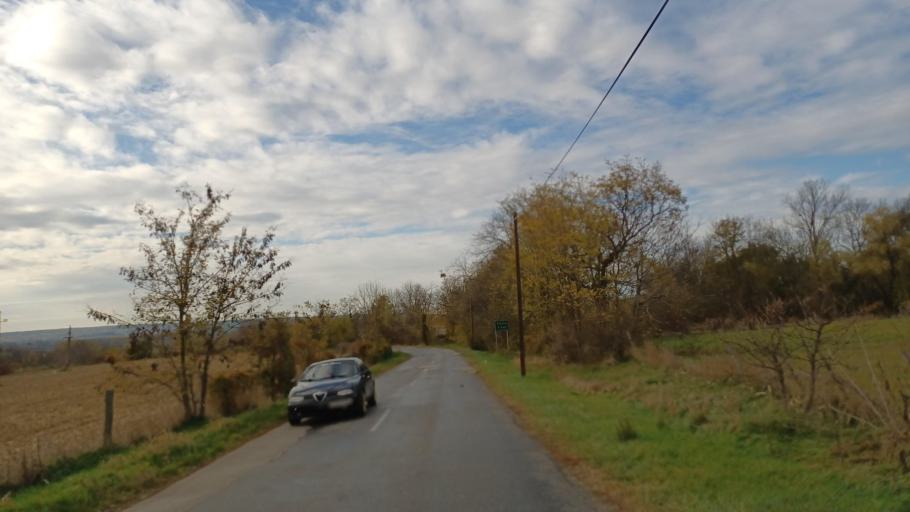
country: HU
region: Fejer
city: Cece
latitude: 46.7185
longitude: 18.6610
